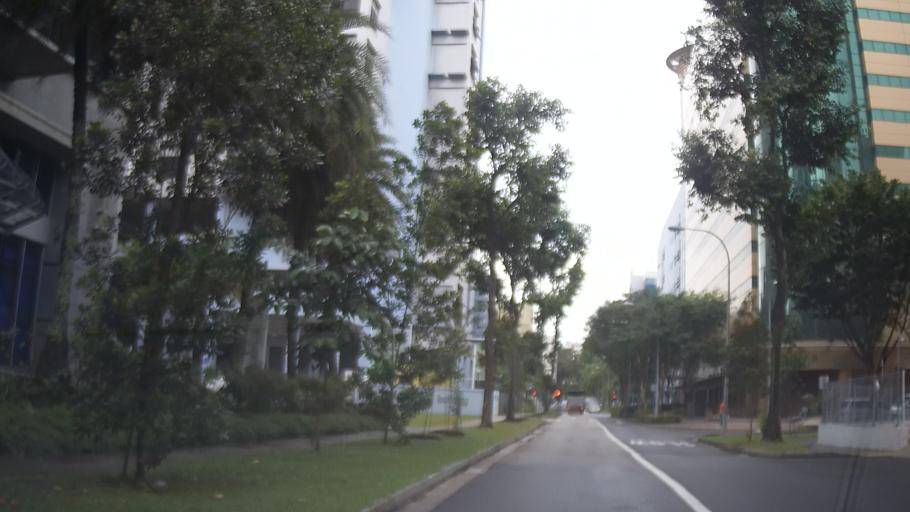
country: SG
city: Singapore
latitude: 1.3287
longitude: 103.8766
